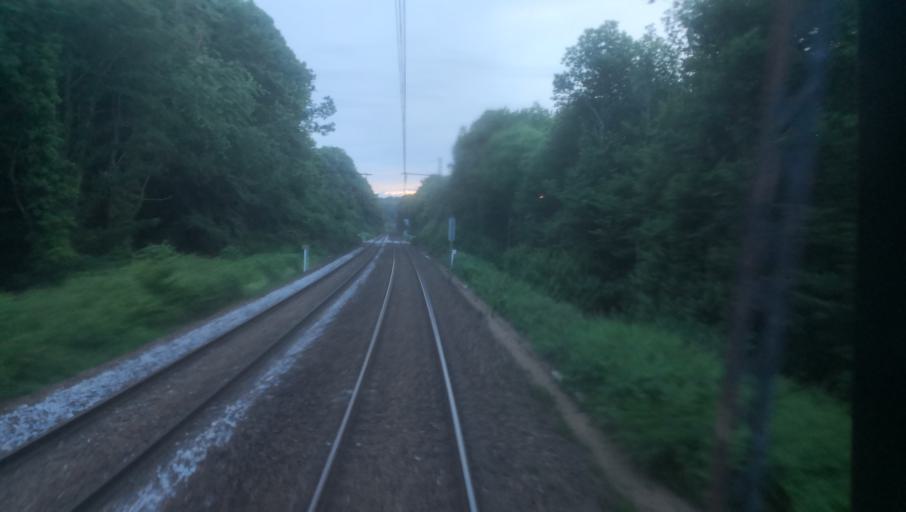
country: FR
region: Limousin
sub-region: Departement de la Haute-Vienne
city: Bessines-sur-Gartempe
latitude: 46.0630
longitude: 1.4446
